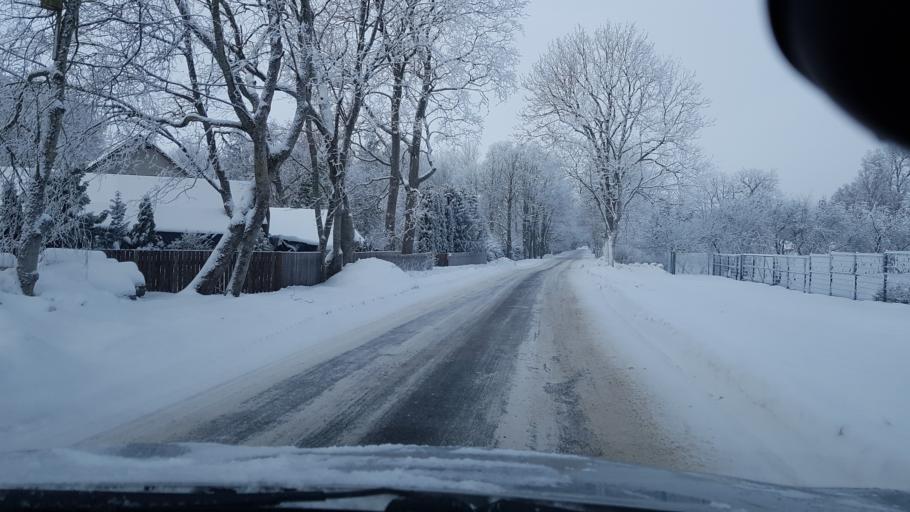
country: EE
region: Harju
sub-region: Keila linn
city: Keila
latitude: 59.3240
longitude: 24.4513
